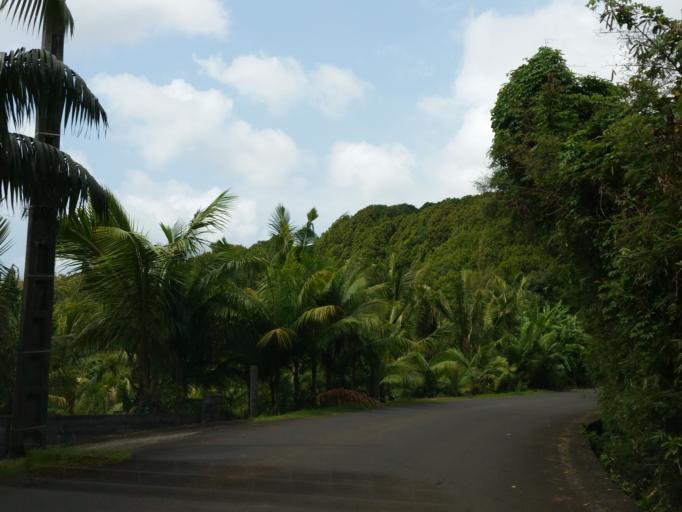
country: RE
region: Reunion
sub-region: Reunion
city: Sainte-Suzanne
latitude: -20.9262
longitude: 55.6050
